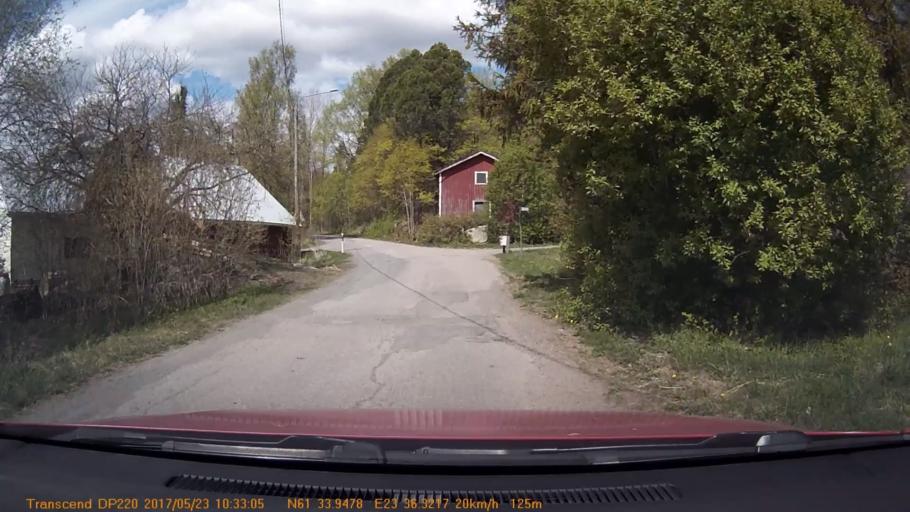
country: FI
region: Pirkanmaa
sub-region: Tampere
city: Yloejaervi
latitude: 61.5658
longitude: 23.6054
